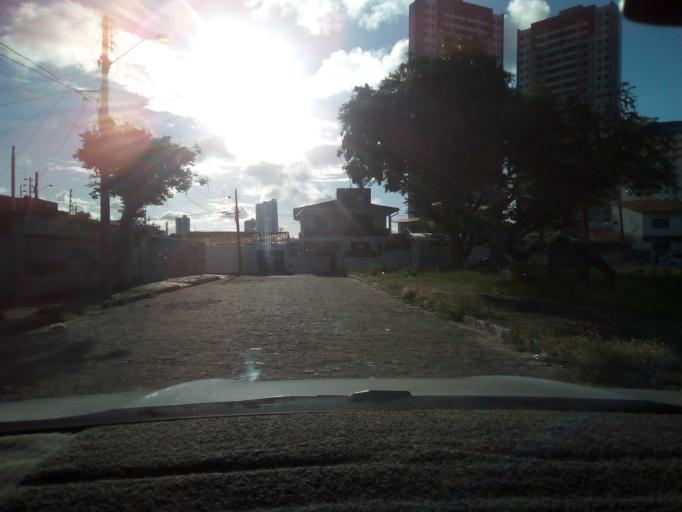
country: BR
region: Paraiba
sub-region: Joao Pessoa
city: Joao Pessoa
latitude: -7.1112
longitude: -34.8390
